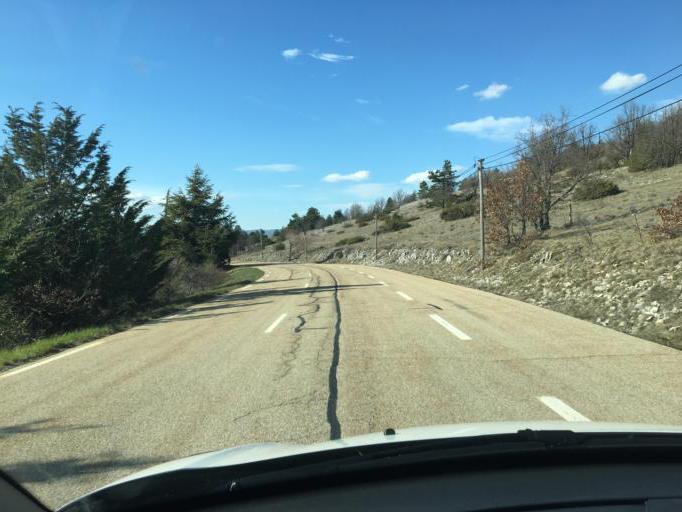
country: FR
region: Provence-Alpes-Cote d'Azur
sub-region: Departement du Vaucluse
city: Sault
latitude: 44.0144
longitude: 5.4745
